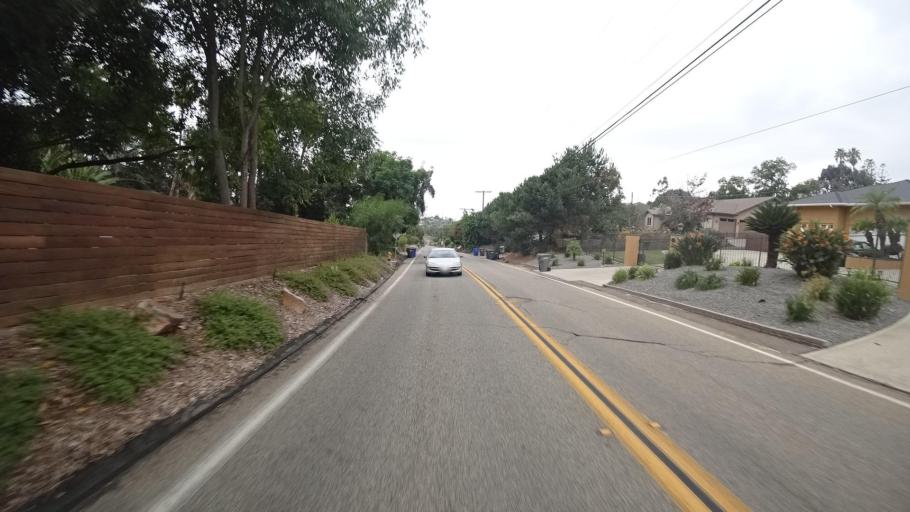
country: US
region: California
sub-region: San Diego County
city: Casa de Oro-Mount Helix
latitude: 32.7611
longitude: -116.9812
